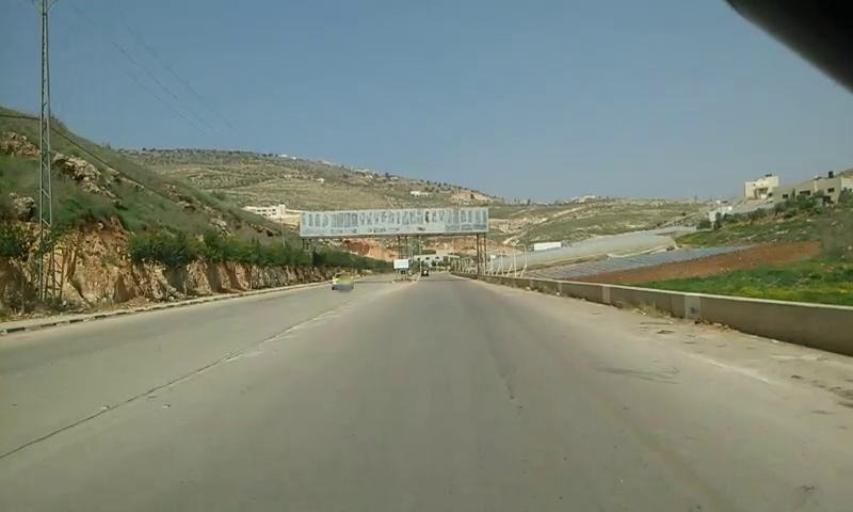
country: PS
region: West Bank
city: Tubas
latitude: 32.3046
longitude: 35.3638
